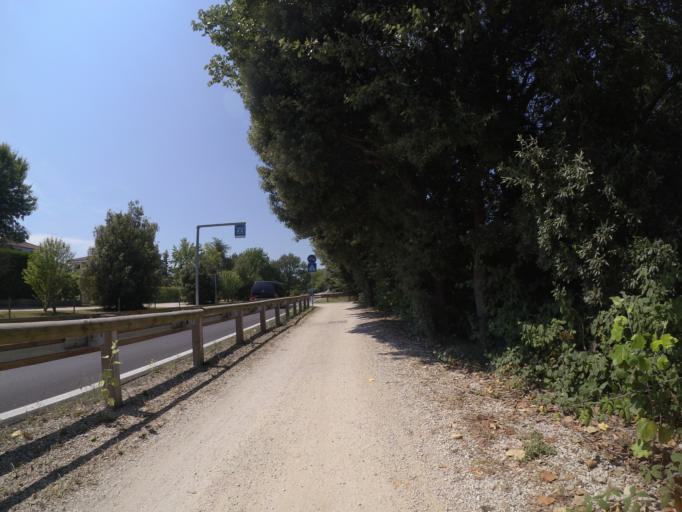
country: IT
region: Veneto
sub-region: Provincia di Venezia
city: Bibione
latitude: 45.6491
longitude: 13.0586
